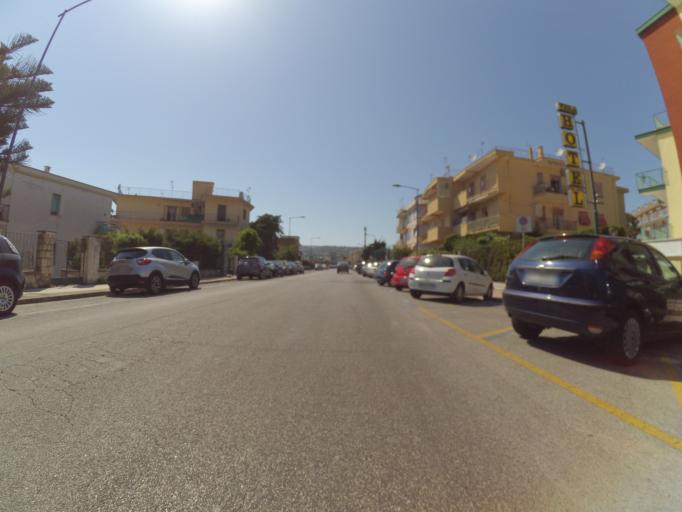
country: IT
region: Latium
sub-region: Provincia di Latina
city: Gaeta
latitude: 41.2111
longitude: 13.5691
